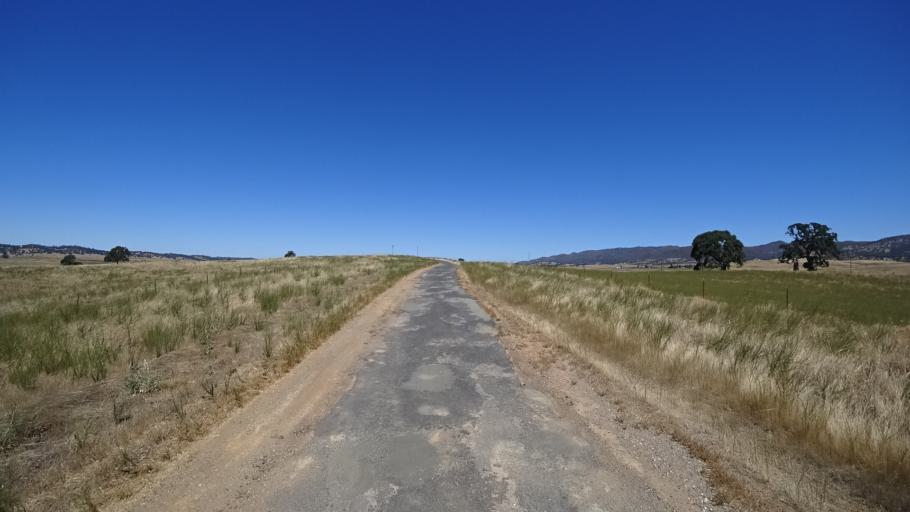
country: US
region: California
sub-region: Calaveras County
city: Copperopolis
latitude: 38.0375
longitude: -120.7265
